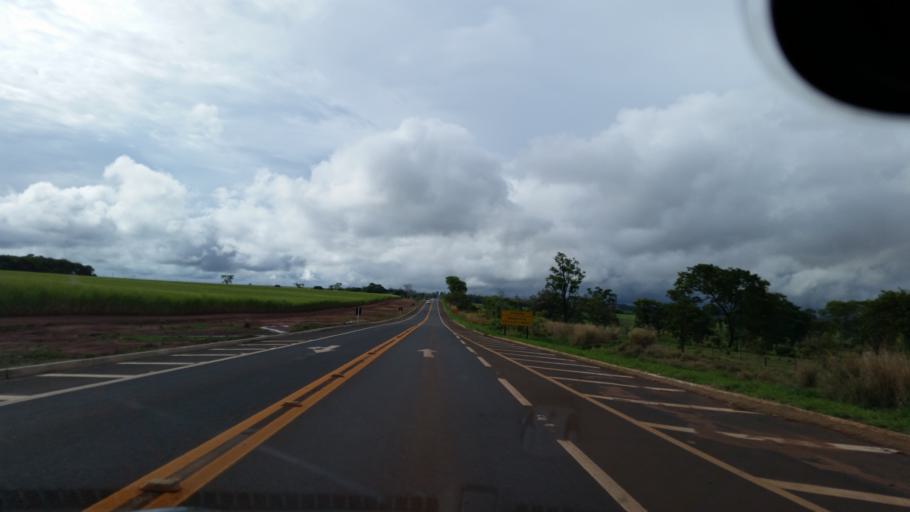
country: BR
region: Minas Gerais
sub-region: Tupaciguara
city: Tupaciguara
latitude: -18.7481
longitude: -48.6128
